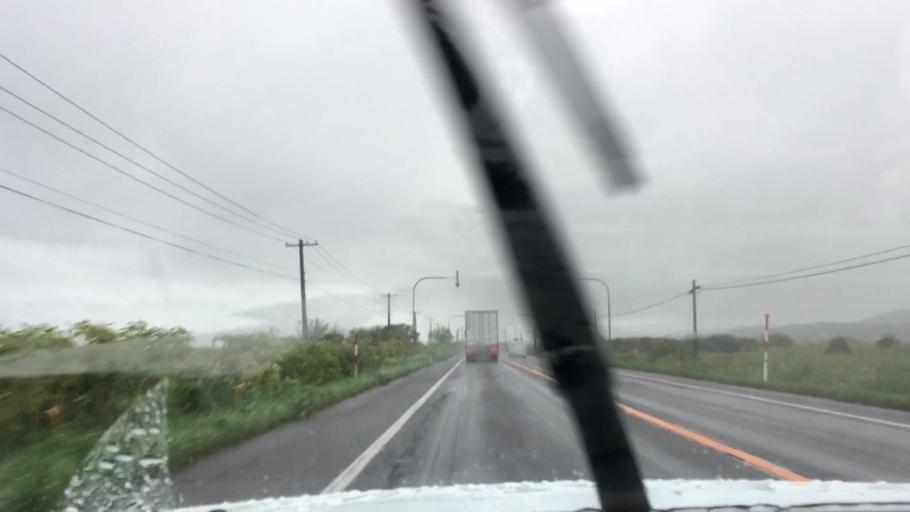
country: JP
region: Hokkaido
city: Niseko Town
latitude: 42.4298
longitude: 140.3179
